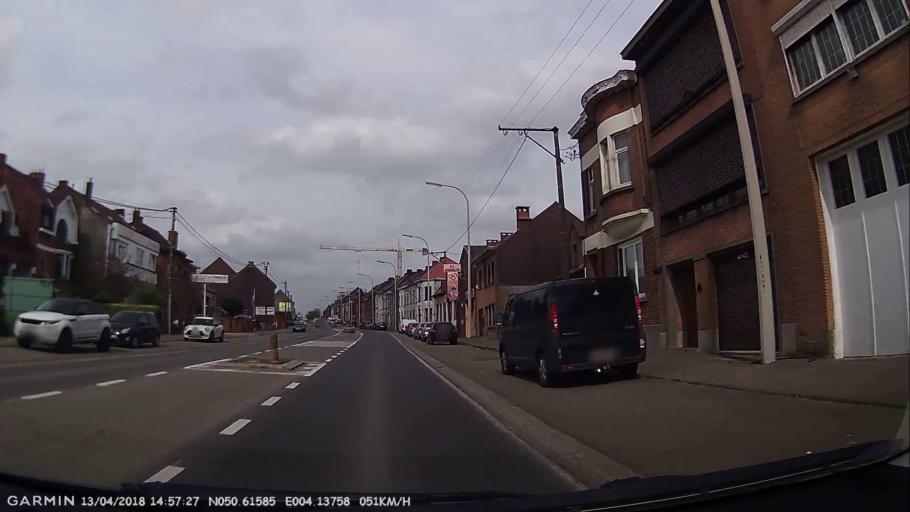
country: BE
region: Wallonia
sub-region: Province du Hainaut
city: Braine-le-Comte
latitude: 50.6158
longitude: 4.1376
